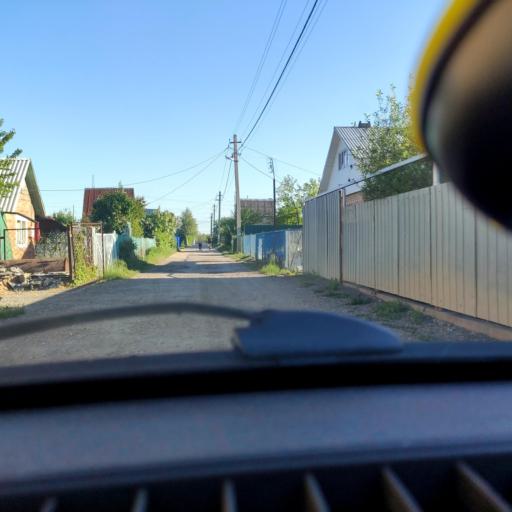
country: RU
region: Samara
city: Tol'yatti
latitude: 53.5916
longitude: 49.3149
